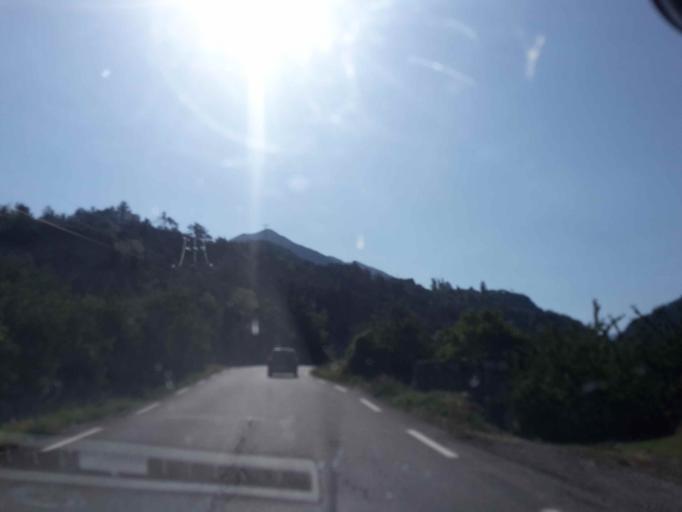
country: FR
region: Provence-Alpes-Cote d'Azur
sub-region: Departement des Hautes-Alpes
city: Guillestre
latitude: 44.6440
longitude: 6.6595
